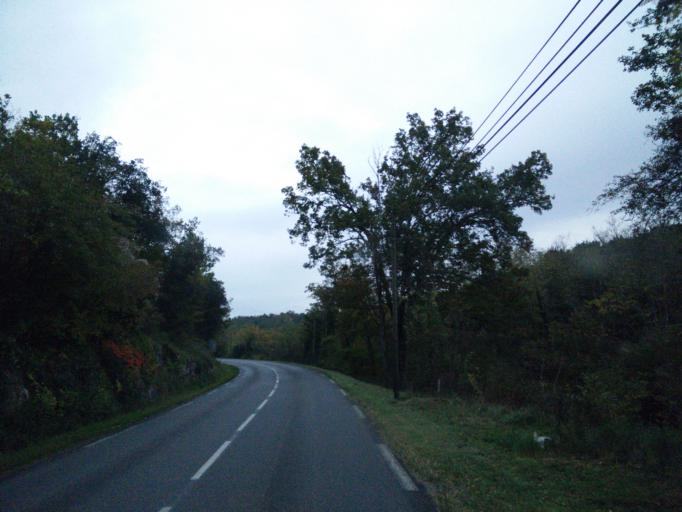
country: FR
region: Aquitaine
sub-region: Departement de la Dordogne
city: Carsac-Aillac
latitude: 44.7864
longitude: 1.3127
